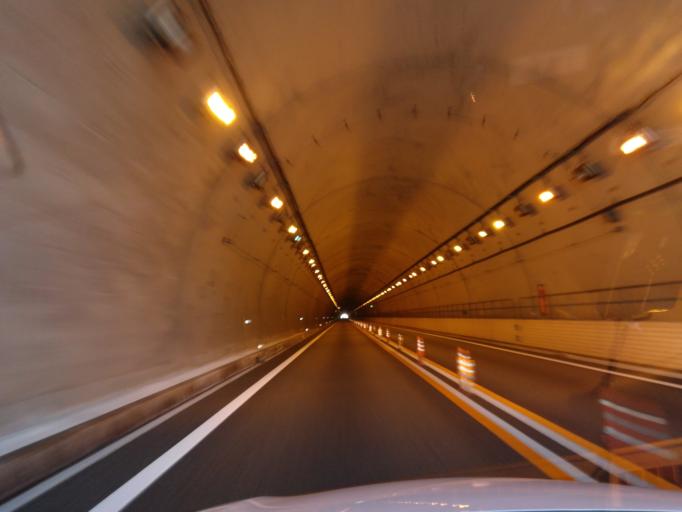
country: JP
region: Tokushima
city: Ikedacho
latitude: 34.0239
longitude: 133.7894
